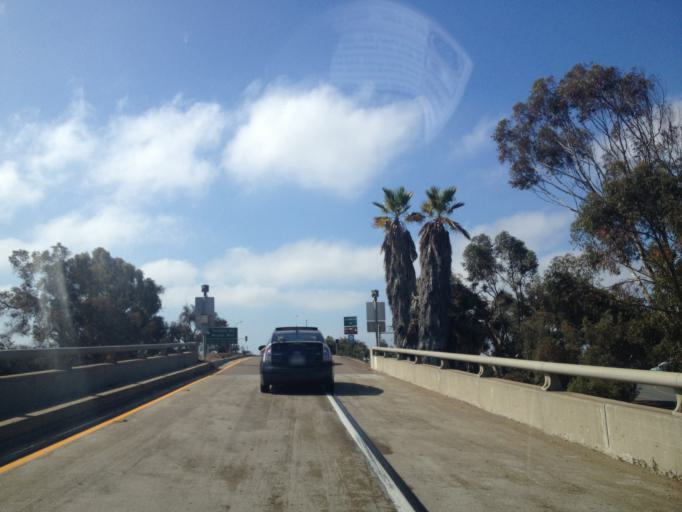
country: US
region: California
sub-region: San Diego County
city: San Diego
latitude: 32.7710
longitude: -117.2074
